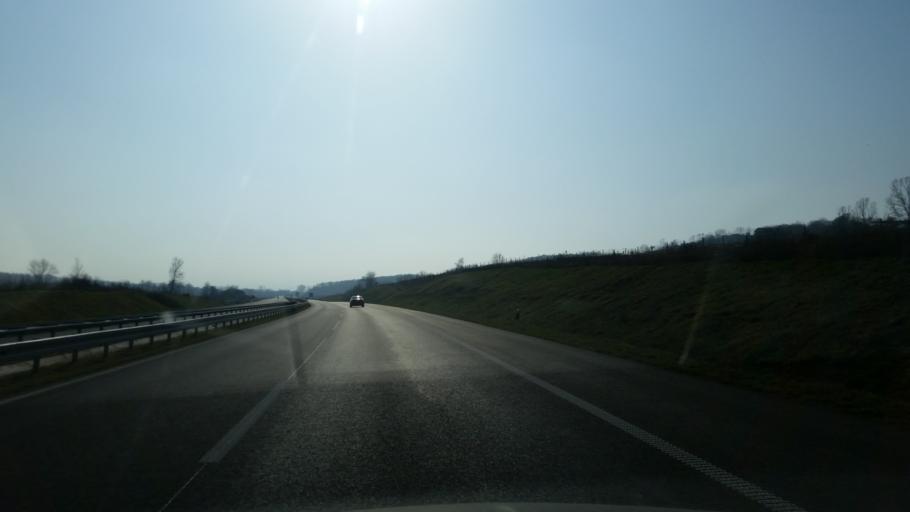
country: RS
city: Prislonica
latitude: 43.9442
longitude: 20.3999
